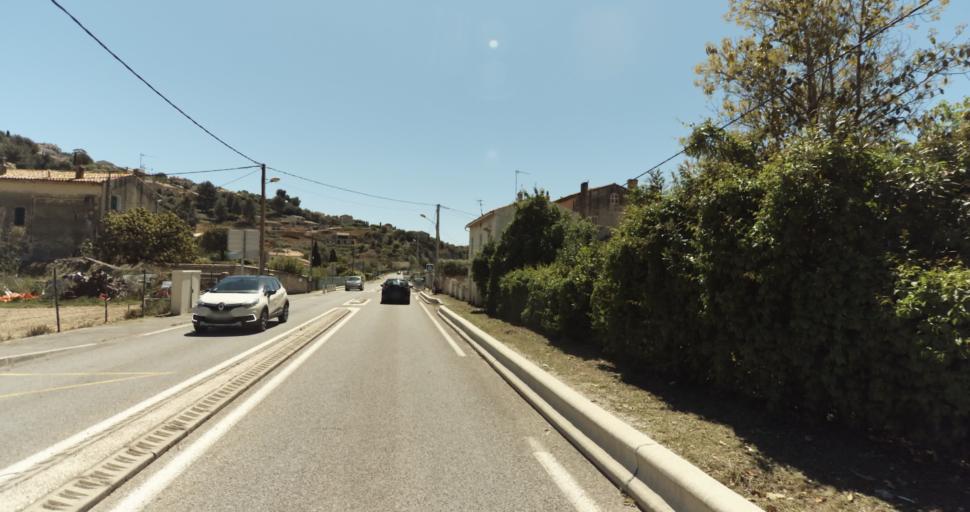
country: FR
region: Provence-Alpes-Cote d'Azur
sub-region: Departement du Var
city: Ollioules
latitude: 43.1424
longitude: 5.8477
